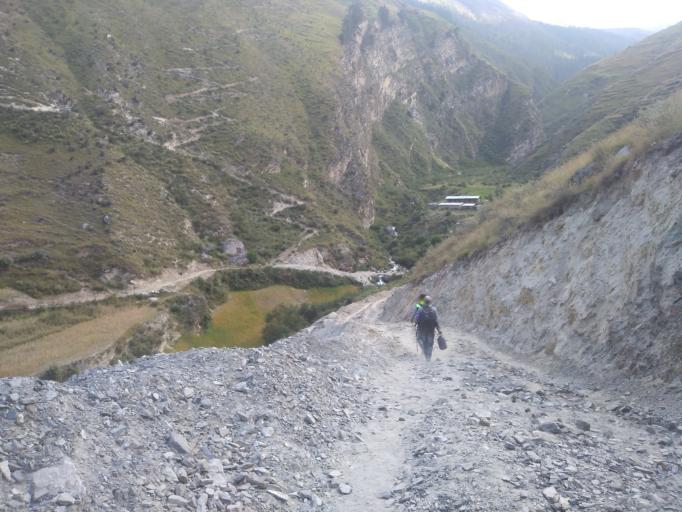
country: NP
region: Western Region
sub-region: Dhawalagiri Zone
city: Jomsom
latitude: 28.8808
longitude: 82.9911
